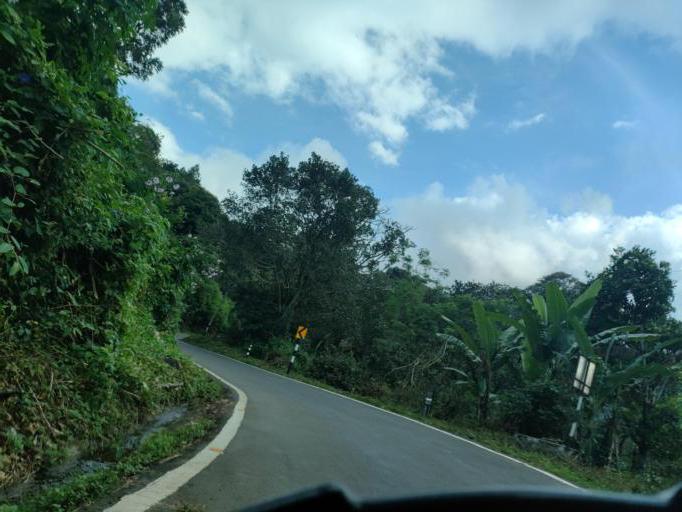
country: IN
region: Tamil Nadu
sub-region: Dindigul
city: Kodaikanal
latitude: 10.2685
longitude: 77.5338
